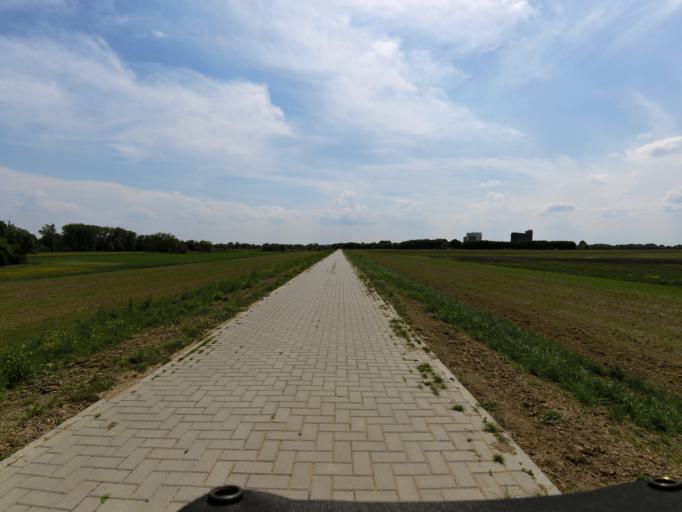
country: NL
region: North Brabant
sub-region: Gemeente Woudrichem
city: Woudrichem
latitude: 51.8051
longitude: 5.0564
